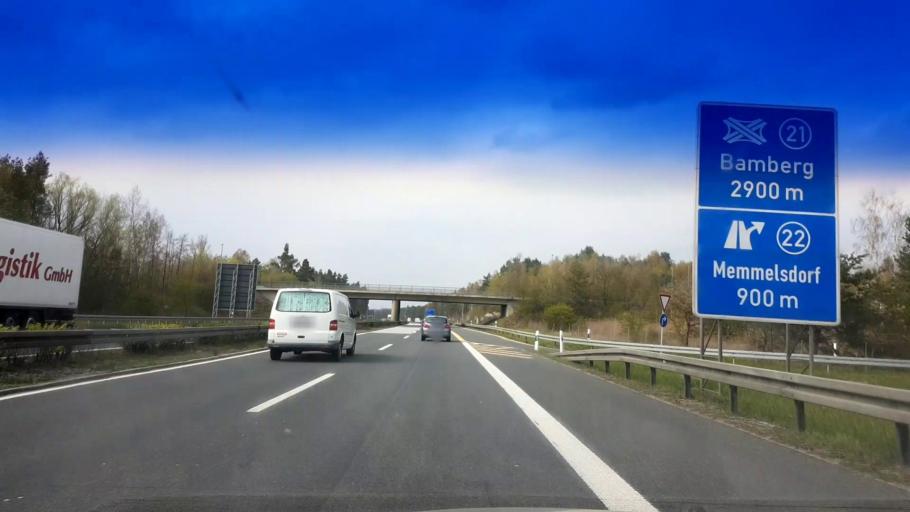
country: DE
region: Bavaria
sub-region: Upper Franconia
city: Memmelsdorf
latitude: 49.9122
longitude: 10.9404
